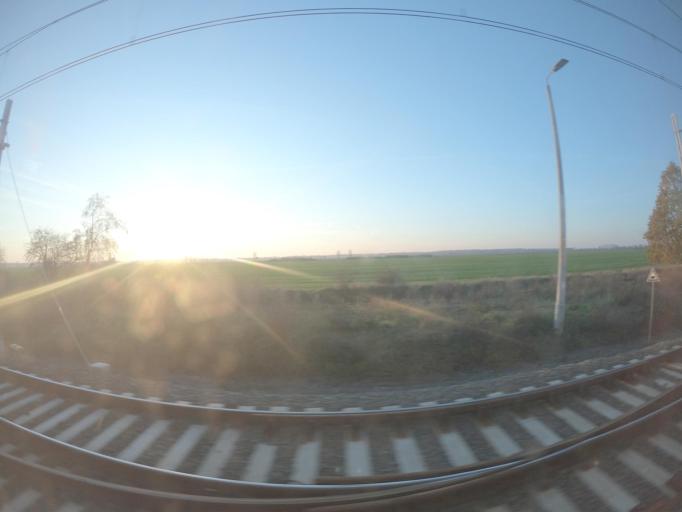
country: PL
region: Lubusz
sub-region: Powiat slubicki
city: Gorzyca
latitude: 52.5235
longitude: 14.6506
